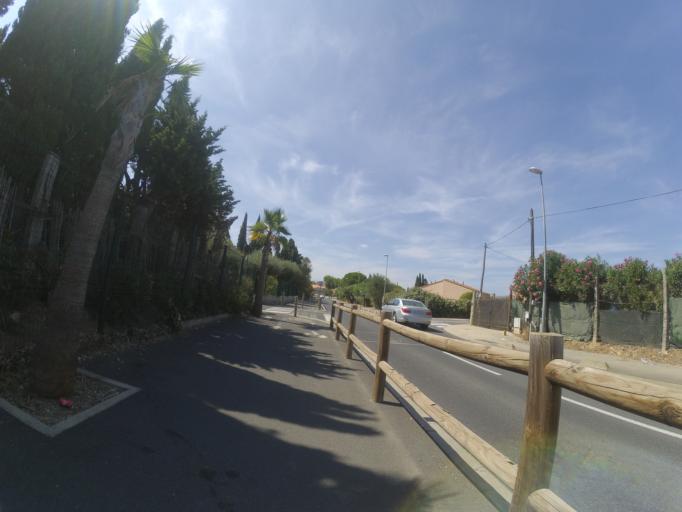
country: FR
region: Languedoc-Roussillon
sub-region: Departement des Pyrenees-Orientales
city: Rivesaltes
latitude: 42.7757
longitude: 2.8730
